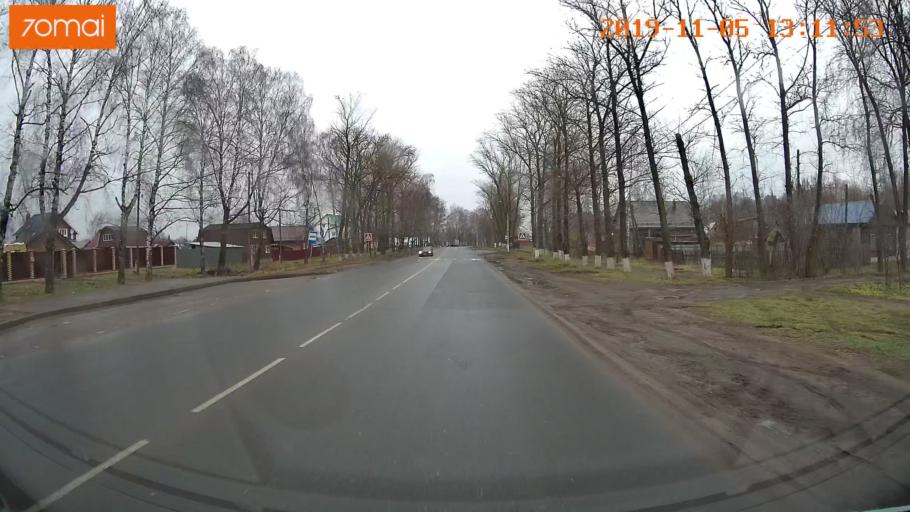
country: RU
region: Ivanovo
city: Shuya
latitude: 56.8580
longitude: 41.3457
